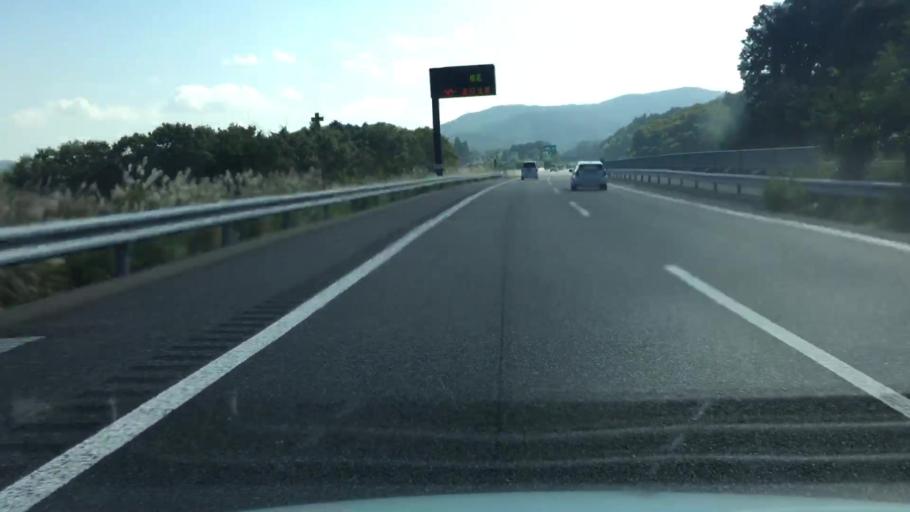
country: JP
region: Ibaraki
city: Iwase
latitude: 36.3478
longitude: 140.1680
